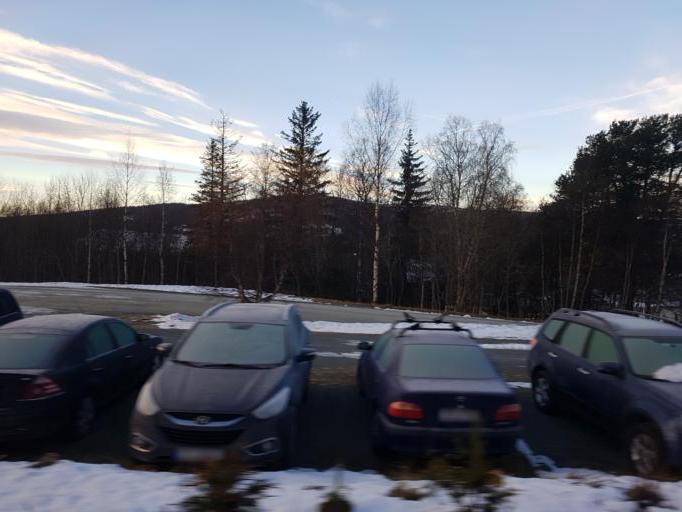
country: NO
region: Sor-Trondelag
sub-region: Rennebu
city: Berkak
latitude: 62.8185
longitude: 10.0152
